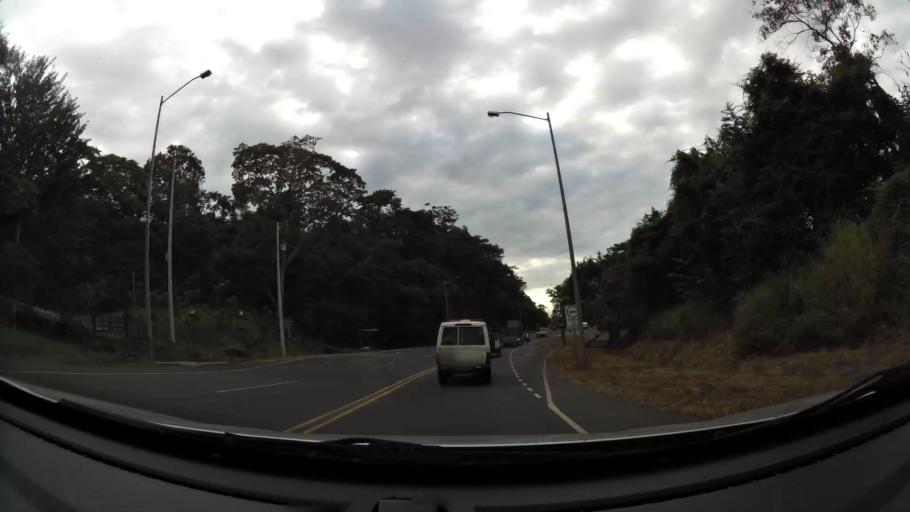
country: CR
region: Puntarenas
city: Esparza
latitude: 9.9164
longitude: -84.7091
